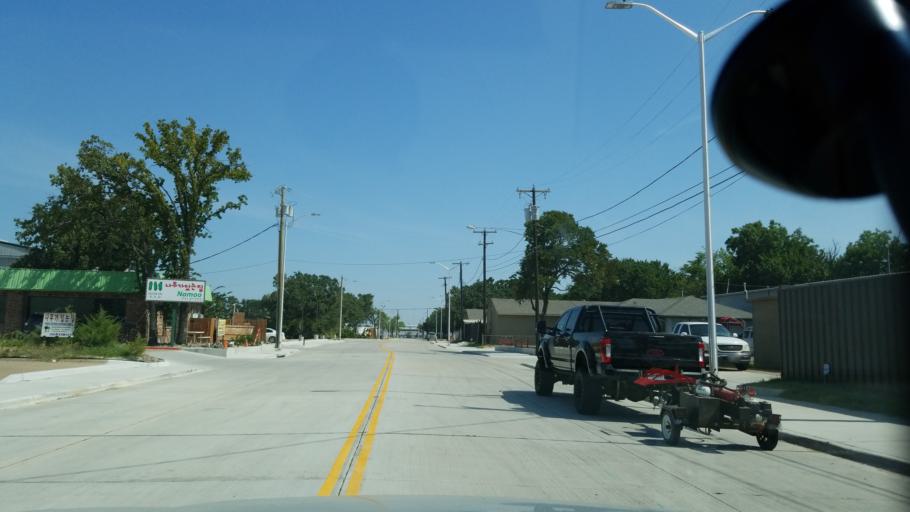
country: US
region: Texas
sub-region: Dallas County
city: Farmers Branch
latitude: 32.8961
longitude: -96.9021
